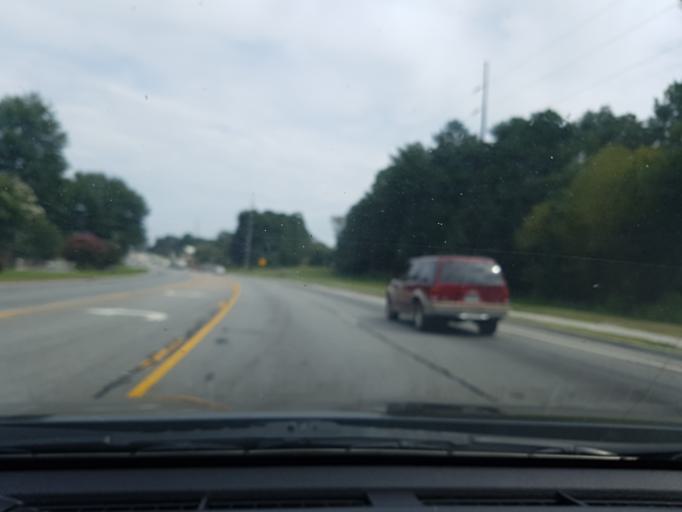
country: US
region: Georgia
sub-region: Gwinnett County
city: Lilburn
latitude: 33.9338
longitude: -84.1565
